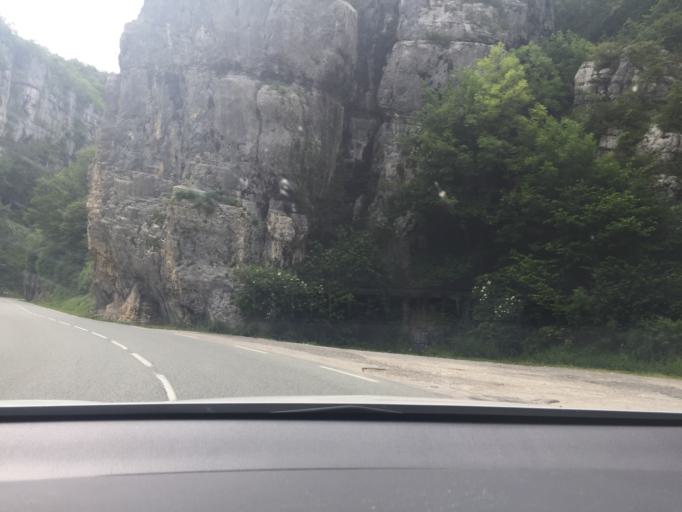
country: FR
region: Rhone-Alpes
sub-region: Departement de l'Isere
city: Saint-Aupre
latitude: 45.3621
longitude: 5.6701
